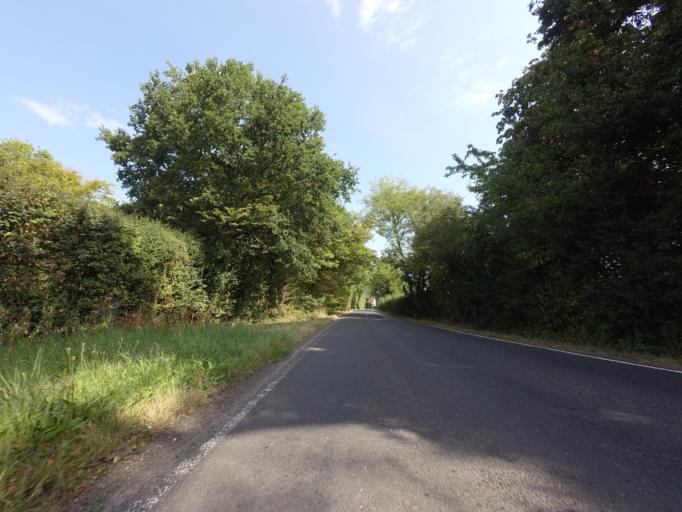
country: GB
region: England
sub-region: Kent
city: Staplehurst
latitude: 51.1293
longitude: 0.5790
